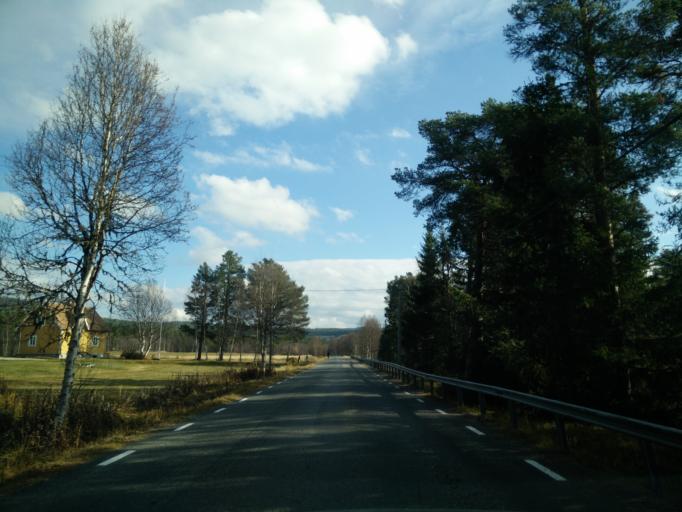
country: SE
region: Jaemtland
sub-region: Are Kommun
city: Are
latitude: 62.5497
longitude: 12.5938
